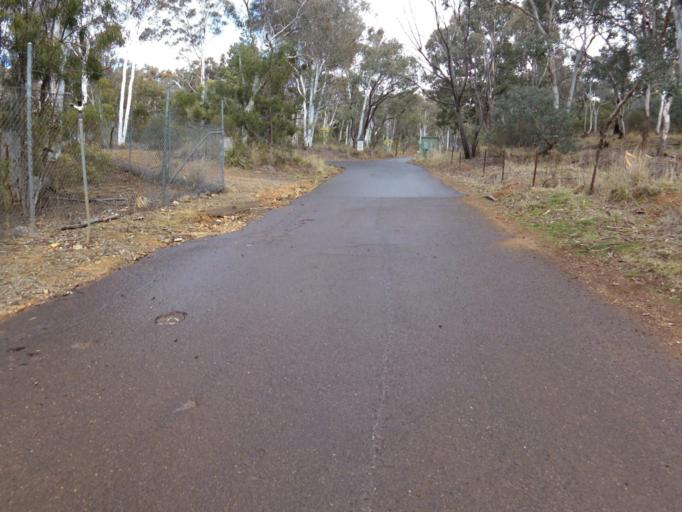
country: AU
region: Australian Capital Territory
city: Acton
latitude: -35.2706
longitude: 149.1079
